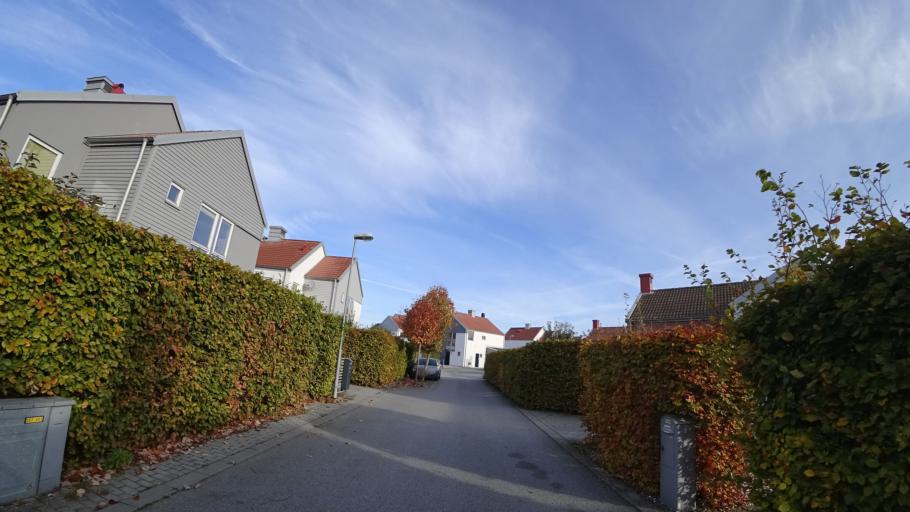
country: SE
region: Skane
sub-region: Staffanstorps Kommun
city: Staffanstorp
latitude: 55.6355
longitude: 13.2184
